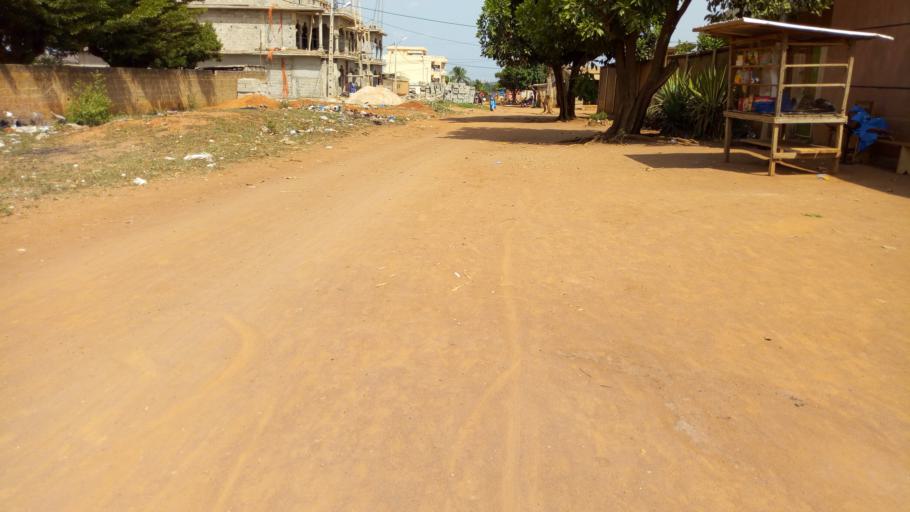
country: CI
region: Vallee du Bandama
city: Bouake
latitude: 7.7102
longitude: -5.0441
